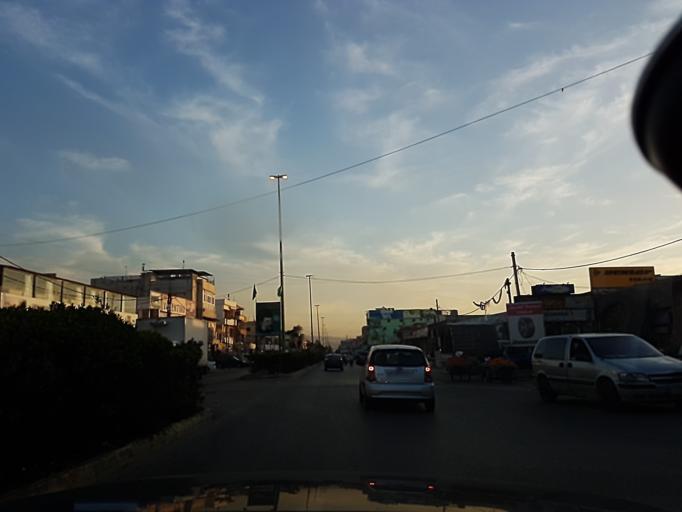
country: LB
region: Beyrouth
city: Beirut
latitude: 33.8426
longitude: 35.4849
